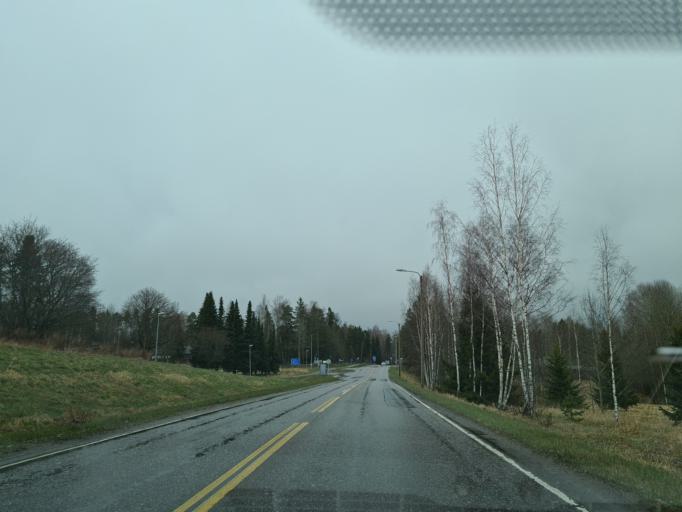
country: FI
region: Uusimaa
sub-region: Helsinki
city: Kirkkonummi
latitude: 60.0930
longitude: 24.4112
